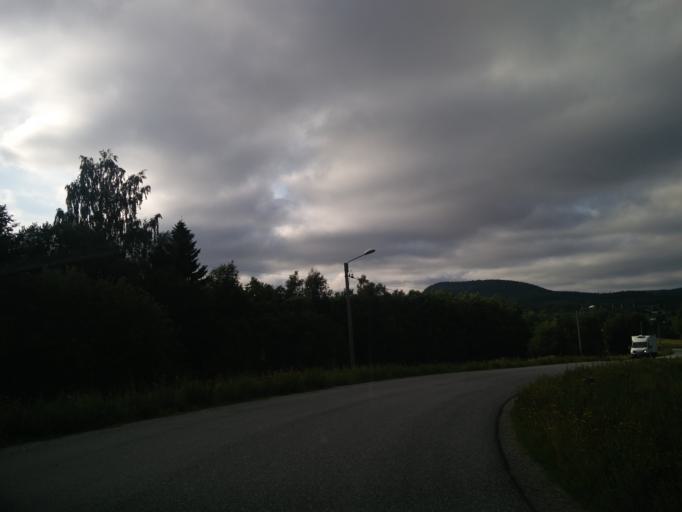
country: SE
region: Vaesternorrland
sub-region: Timra Kommun
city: Timra
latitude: 62.4577
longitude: 17.2540
